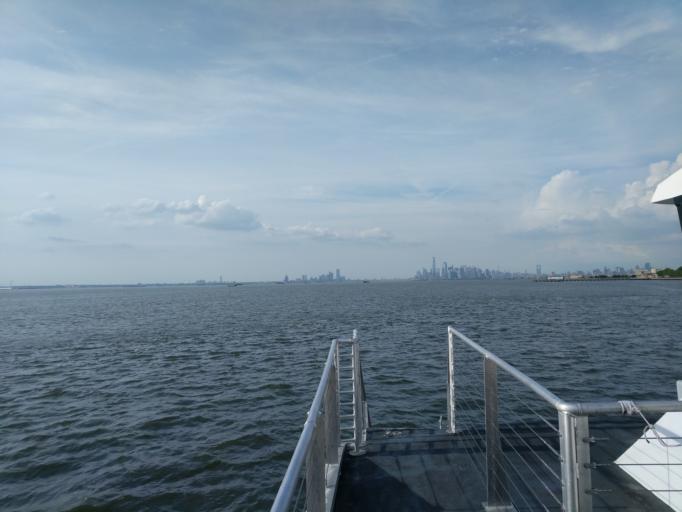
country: US
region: New York
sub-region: Kings County
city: Bensonhurst
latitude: 40.6323
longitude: -74.0440
